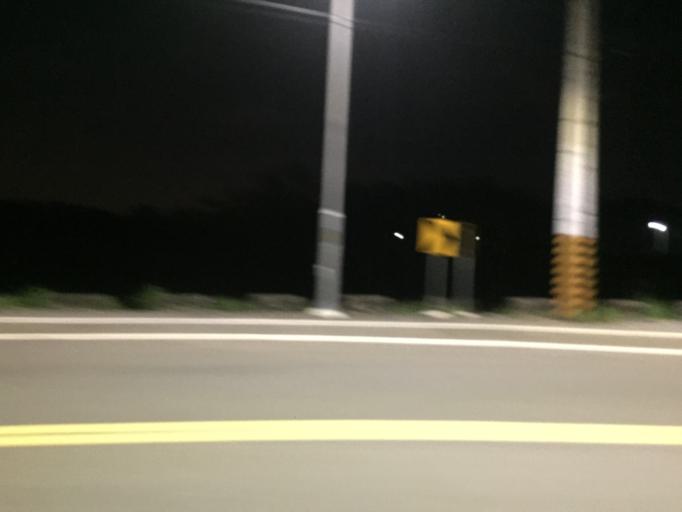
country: TW
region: Taiwan
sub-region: Hsinchu
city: Hsinchu
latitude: 24.7482
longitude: 120.9603
